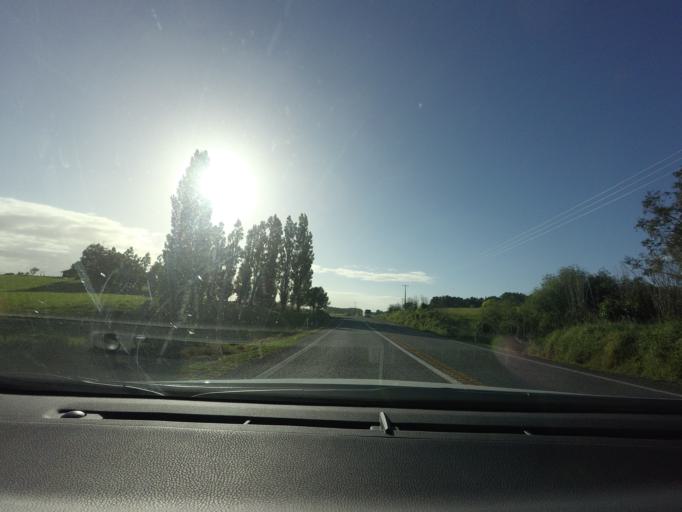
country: NZ
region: Waikato
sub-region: Hauraki District
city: Ngatea
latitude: -37.3885
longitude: 175.4425
